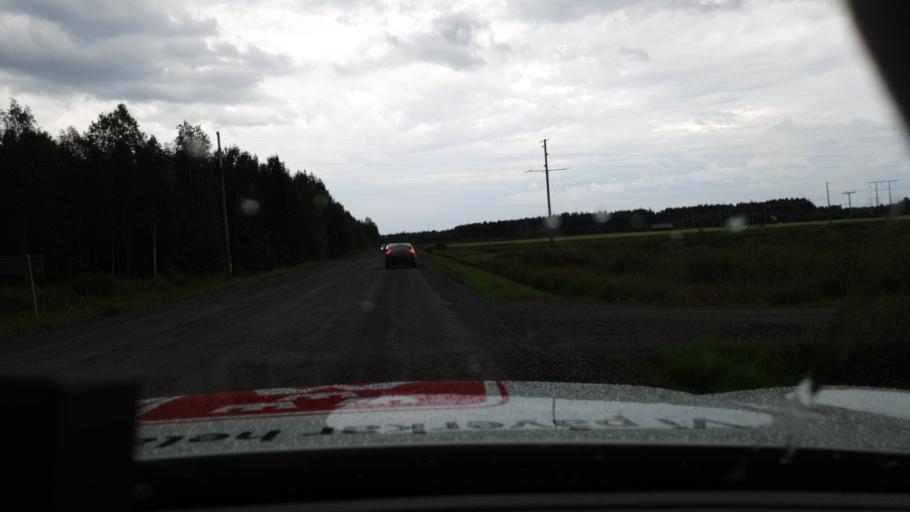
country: SE
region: Norrbotten
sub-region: Bodens Kommun
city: Boden
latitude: 65.8516
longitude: 21.5144
